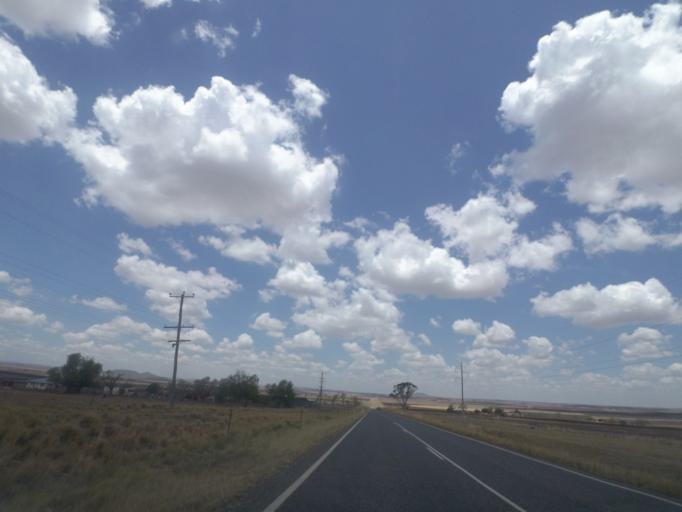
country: AU
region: Queensland
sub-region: Toowoomba
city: Top Camp
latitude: -27.8873
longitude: 151.9719
